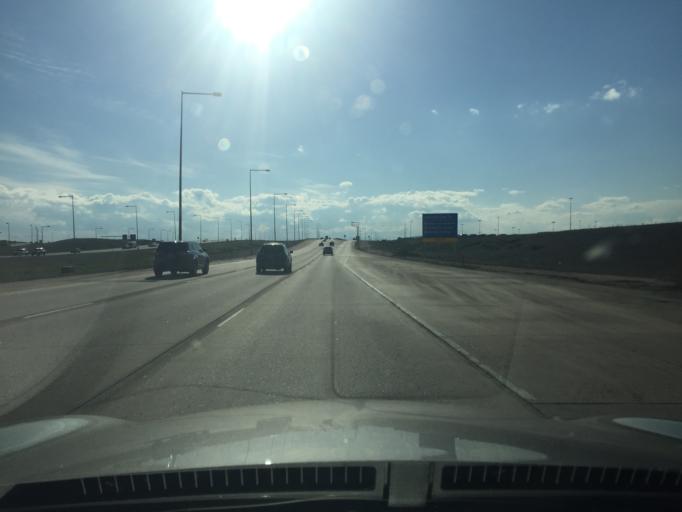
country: US
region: Colorado
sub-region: Weld County
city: Lochbuie
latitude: 39.8342
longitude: -104.6846
